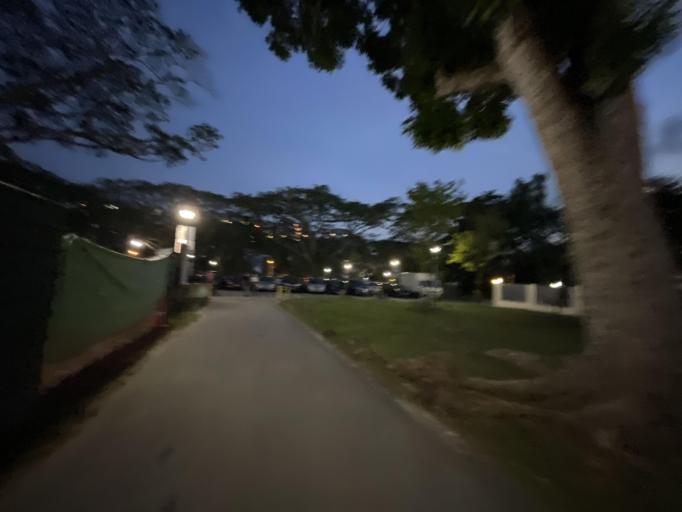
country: MY
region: Johor
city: Kampung Pasir Gudang Baru
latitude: 1.3802
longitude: 103.9596
